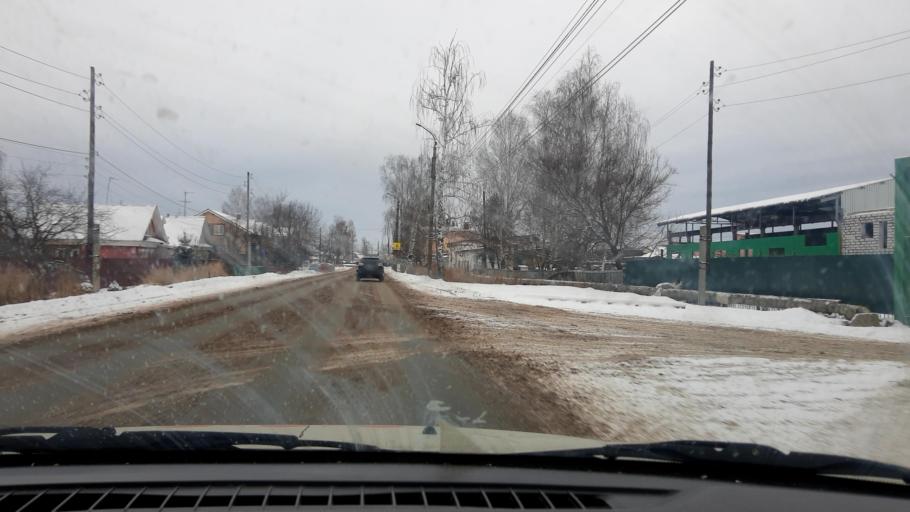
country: RU
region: Nizjnij Novgorod
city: Gorodets
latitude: 56.6522
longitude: 43.4899
